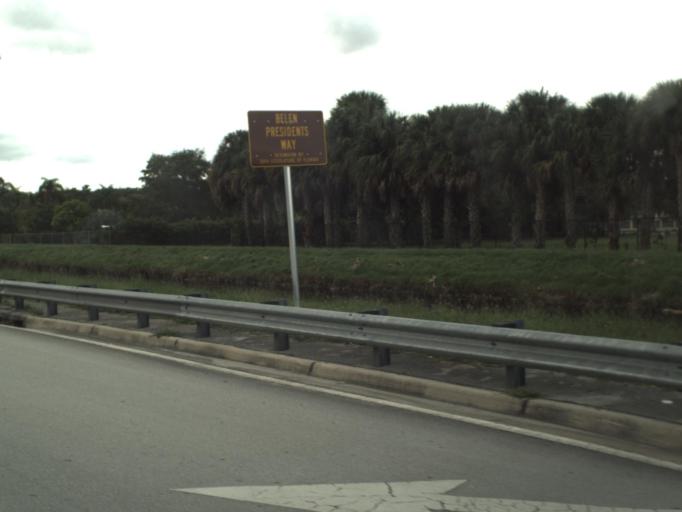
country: US
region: Florida
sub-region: Miami-Dade County
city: Tamiami
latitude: 25.7611
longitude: -80.4020
